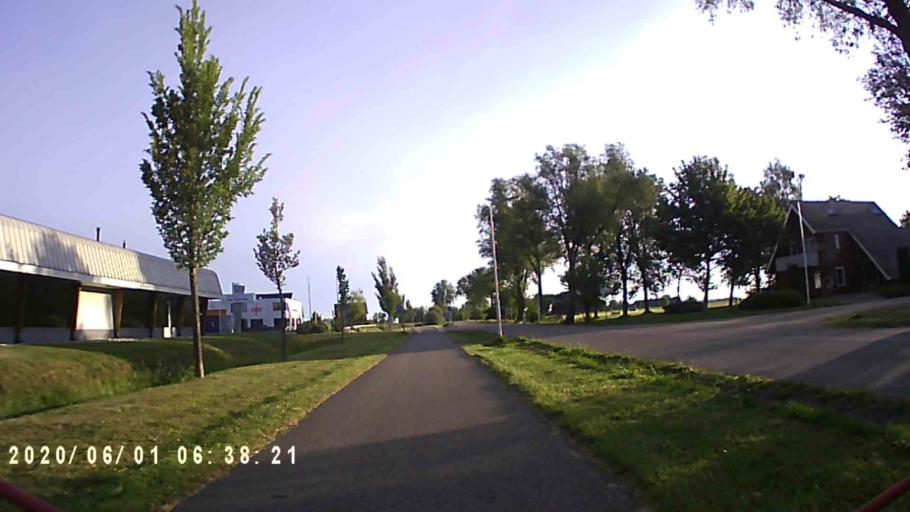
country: NL
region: Friesland
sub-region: Gemeente Kollumerland en Nieuwkruisland
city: Kollum
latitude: 53.2863
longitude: 6.1581
